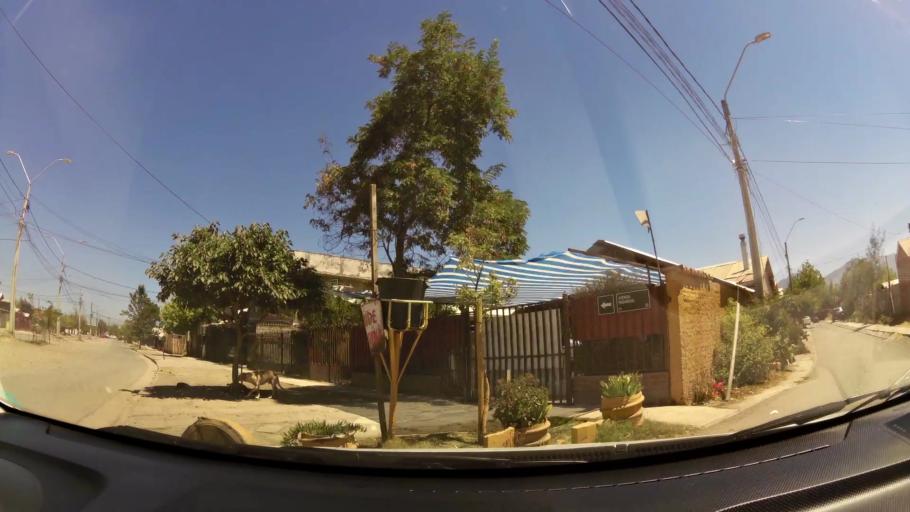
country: CL
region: O'Higgins
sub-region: Provincia de Cachapoal
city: Rancagua
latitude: -34.1634
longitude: -70.7583
